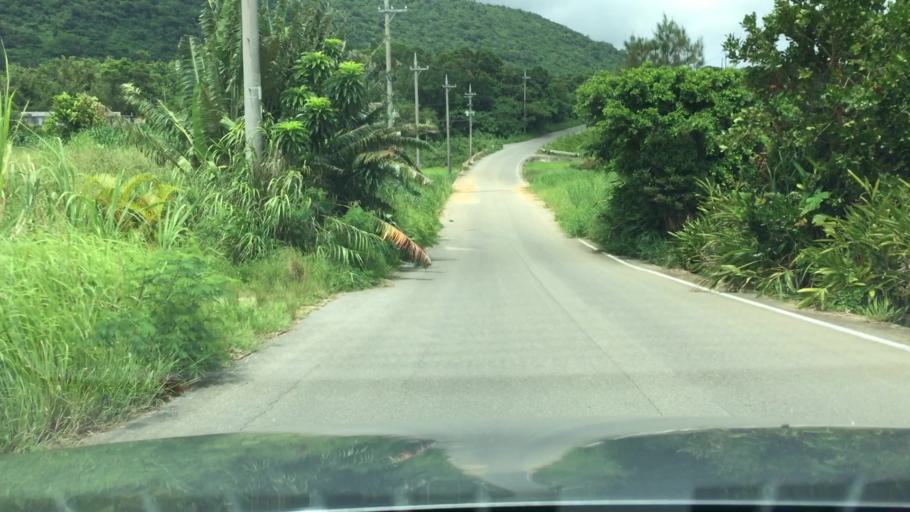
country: JP
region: Okinawa
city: Ishigaki
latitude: 24.3936
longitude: 124.1718
